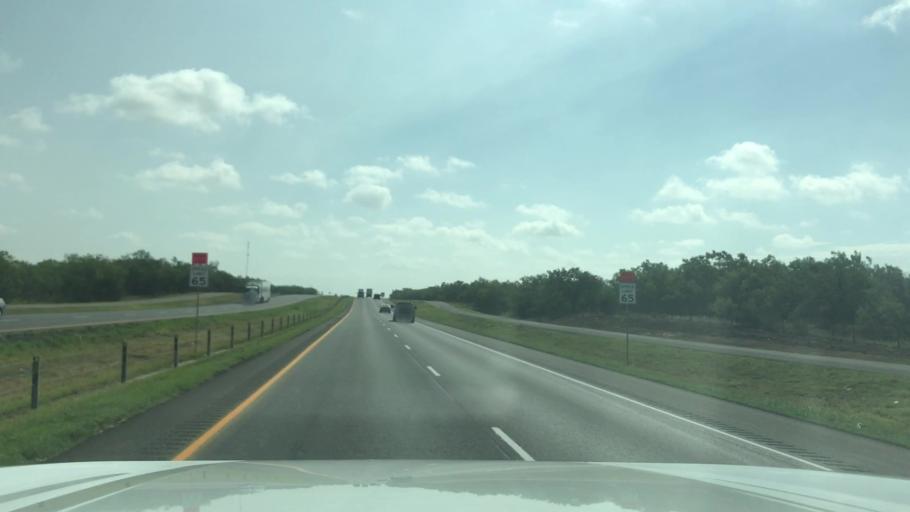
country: US
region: Texas
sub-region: Nolan County
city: Sweetwater
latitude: 32.4919
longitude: -100.3174
